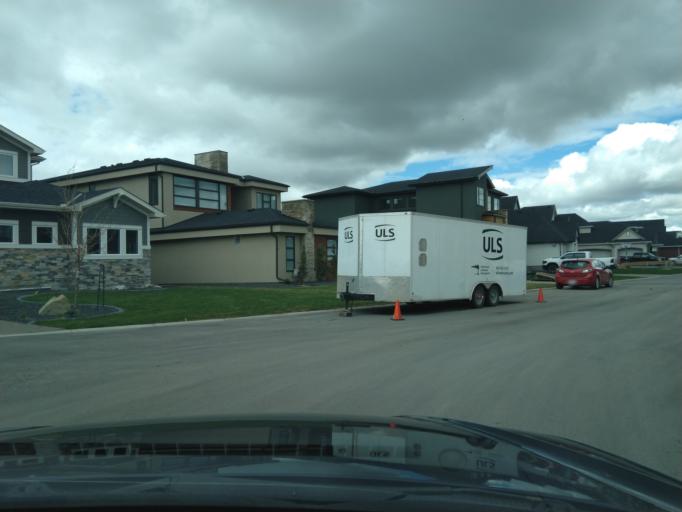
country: CA
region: Alberta
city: Cochrane
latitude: 51.1087
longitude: -114.3956
